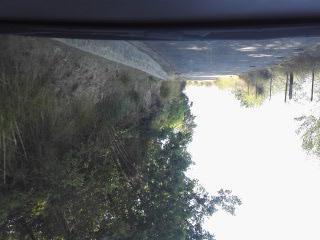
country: IT
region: Calabria
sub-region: Provincia di Reggio Calabria
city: Stilo
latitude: 38.4528
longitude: 16.4616
